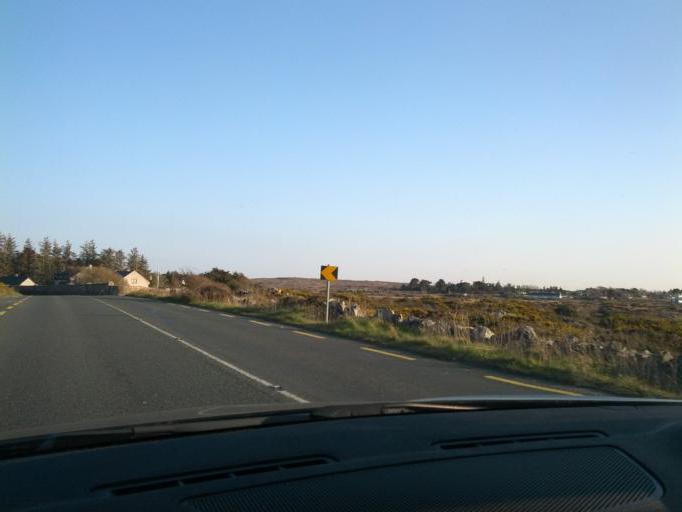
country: IE
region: Connaught
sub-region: County Galway
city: Oughterard
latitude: 53.2818
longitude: -9.5394
